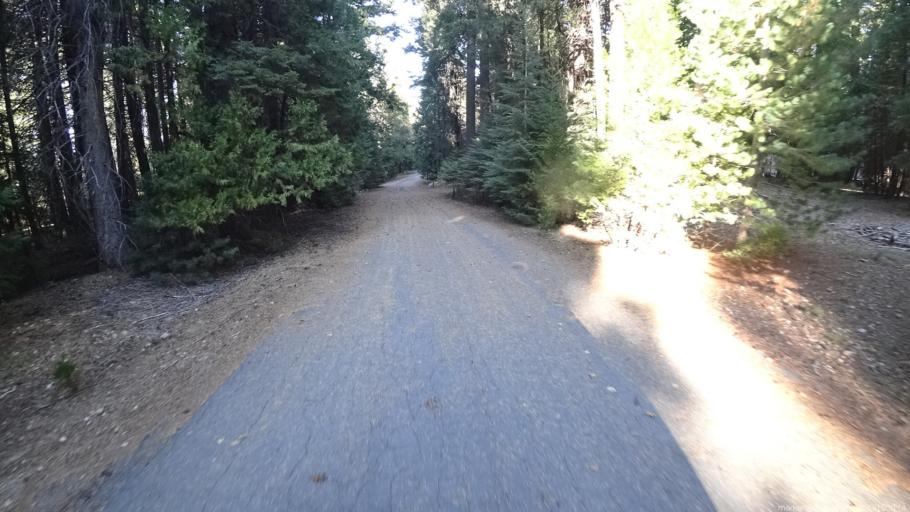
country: US
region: California
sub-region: Shasta County
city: Shingletown
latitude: 40.5510
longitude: -121.7235
